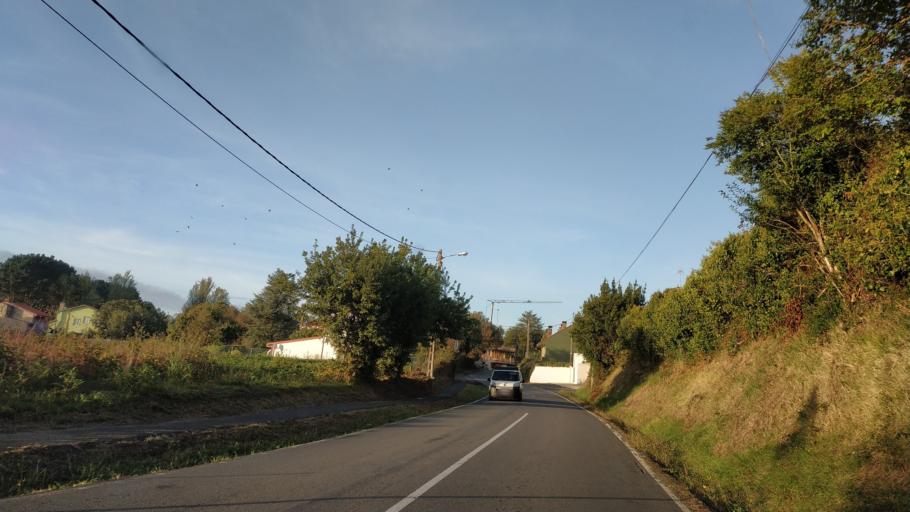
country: ES
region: Galicia
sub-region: Provincia da Coruna
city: Oleiros
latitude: 43.3616
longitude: -8.3419
